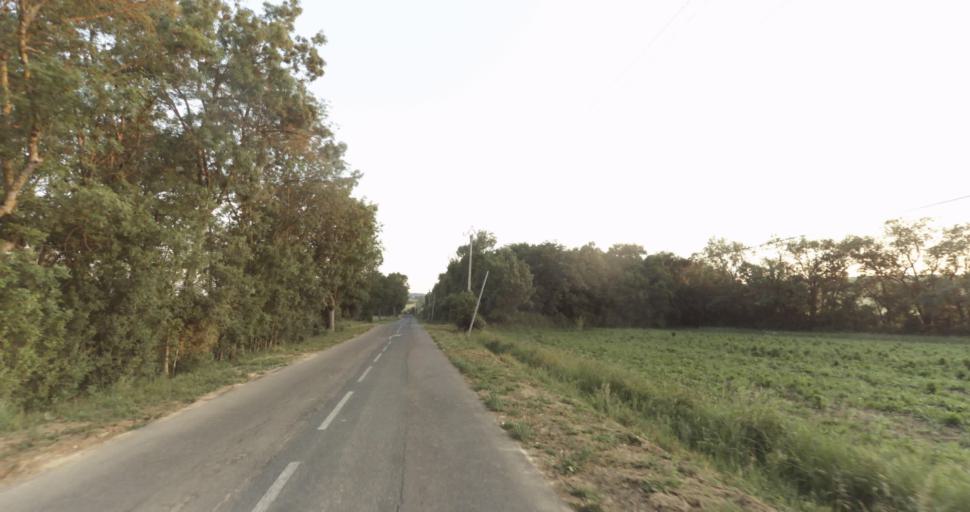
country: FR
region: Midi-Pyrenees
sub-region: Departement du Gers
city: Pujaudran
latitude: 43.6500
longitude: 1.1358
